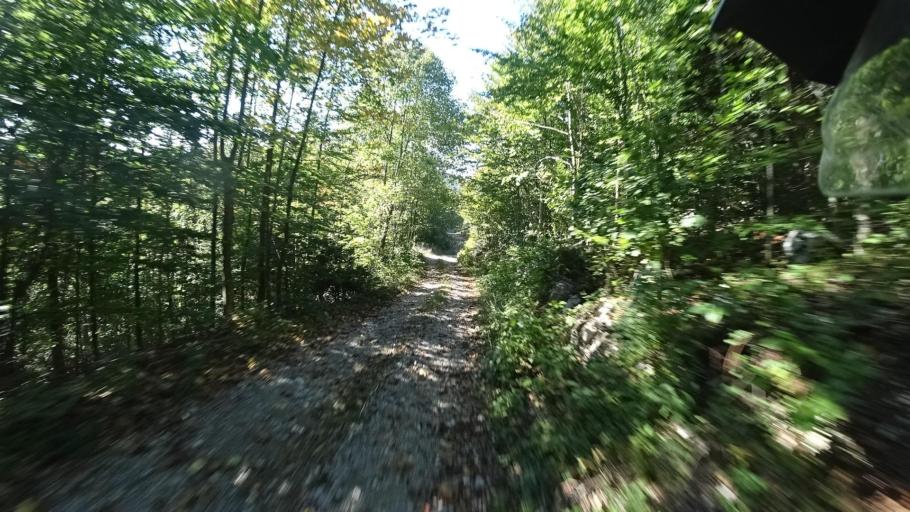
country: HR
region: Primorsko-Goranska
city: Vrbovsko
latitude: 45.2696
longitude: 15.1176
